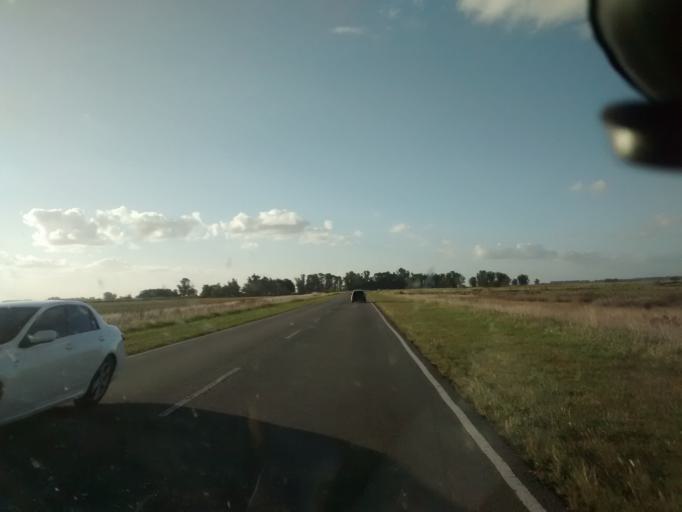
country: AR
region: Buenos Aires
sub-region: Partido de General Belgrano
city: General Belgrano
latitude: -36.1081
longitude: -58.6038
